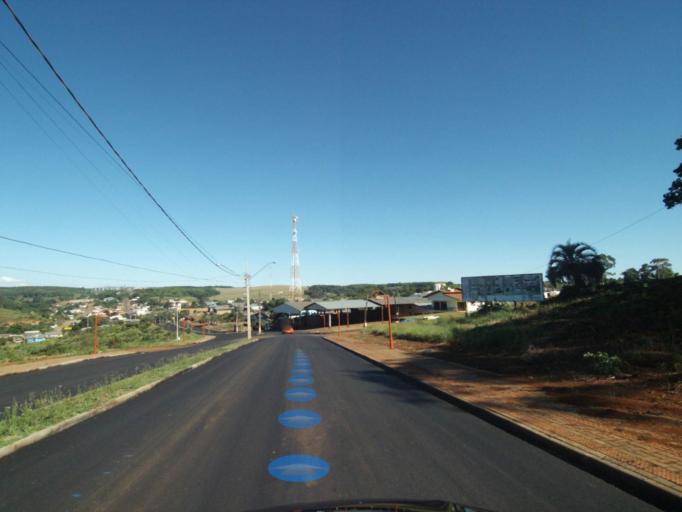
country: BR
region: Parana
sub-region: Coronel Vivida
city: Coronel Vivida
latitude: -26.1407
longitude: -52.3920
